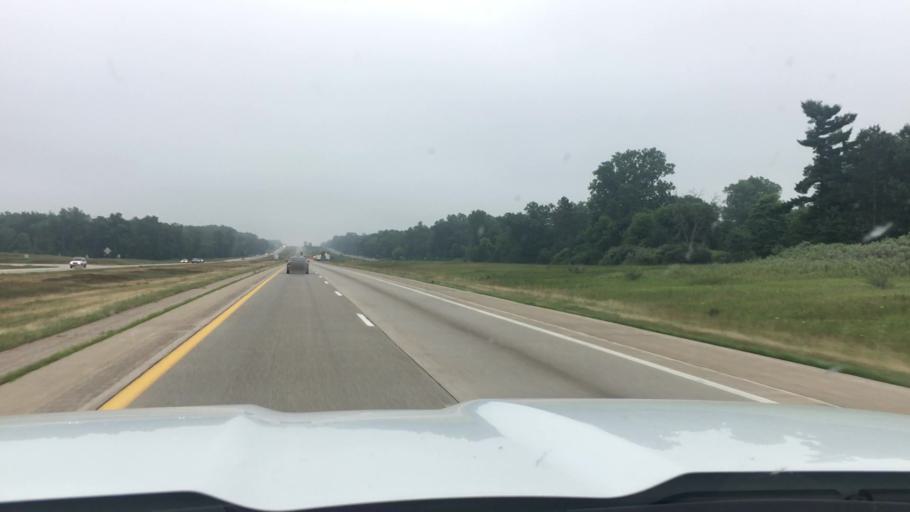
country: US
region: Michigan
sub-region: Ingham County
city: Haslett
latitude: 42.7997
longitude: -84.3493
